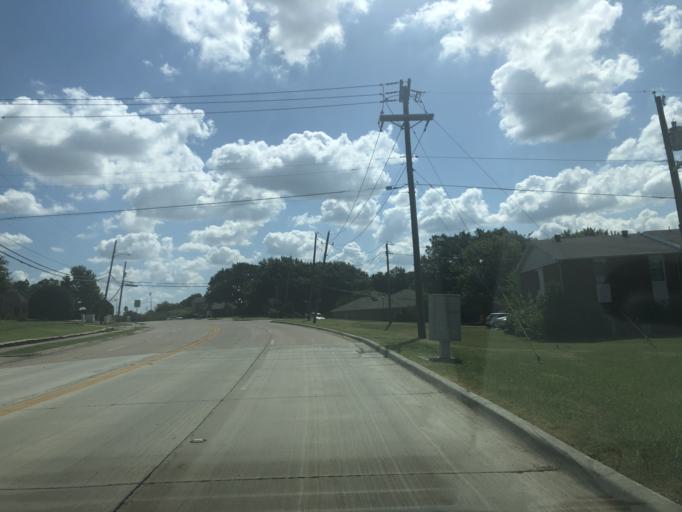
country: US
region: Texas
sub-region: Dallas County
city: Grand Prairie
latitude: 32.7366
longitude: -97.0011
